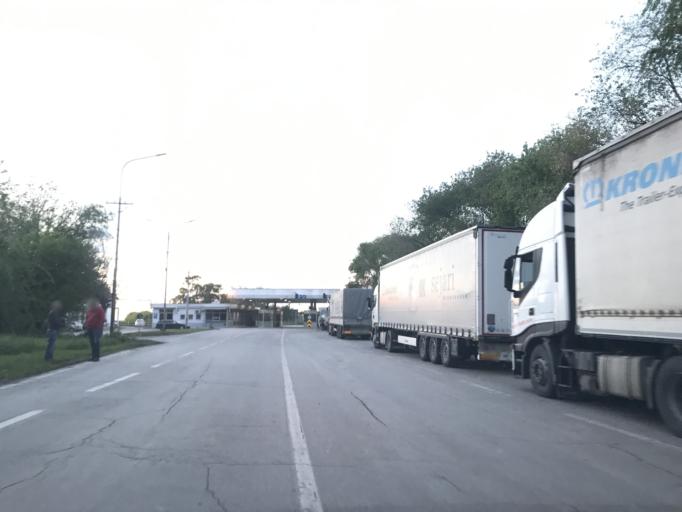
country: RS
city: Srpska Crnja
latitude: 45.7492
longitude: 20.7001
